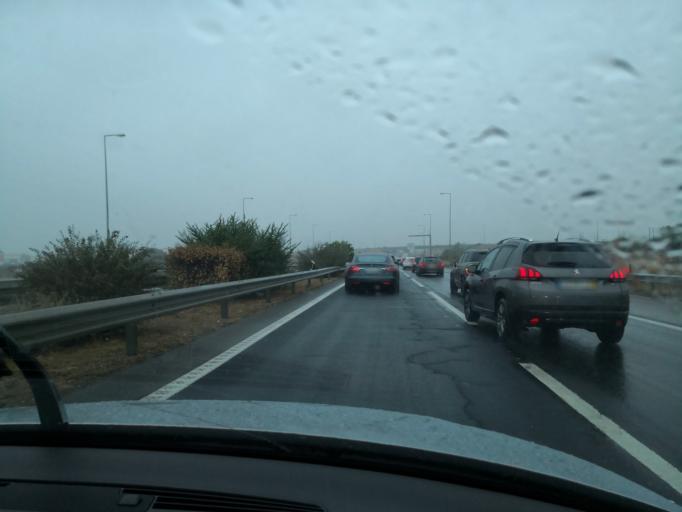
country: PT
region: Setubal
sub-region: Montijo
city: Montijo
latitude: 38.6977
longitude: -8.9400
